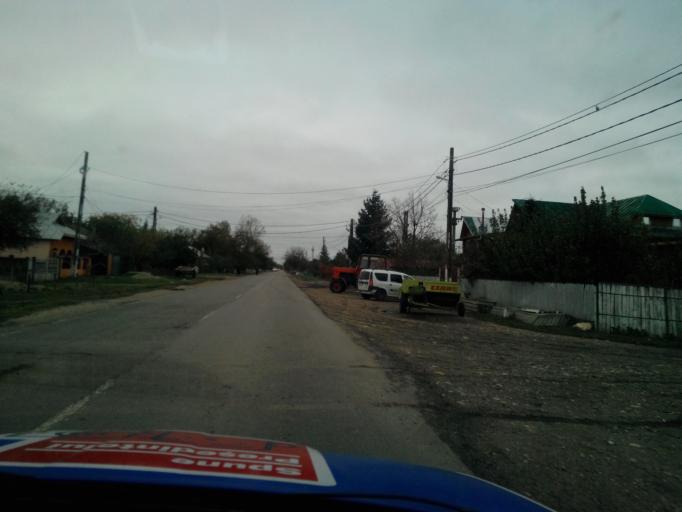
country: RO
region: Giurgiu
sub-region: Comuna Baneasa
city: Baneasa
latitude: 44.0513
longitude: 26.0786
